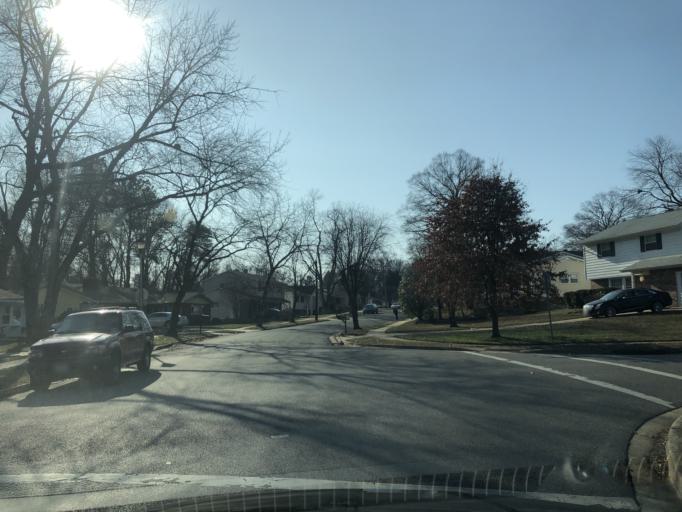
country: US
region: Maryland
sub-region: Anne Arundel County
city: Odenton
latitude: 39.0766
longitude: -76.6899
